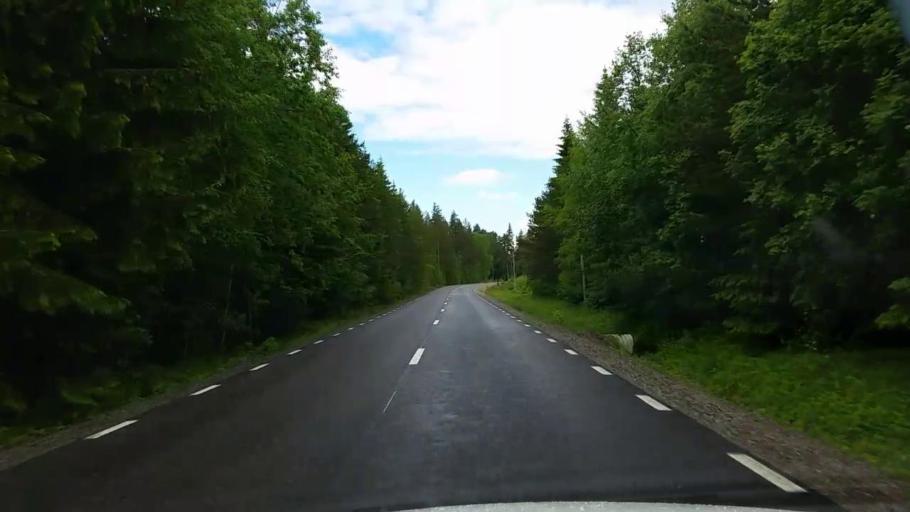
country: SE
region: Gaevleborg
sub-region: Sandvikens Kommun
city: Jarbo
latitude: 60.8511
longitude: 16.4483
